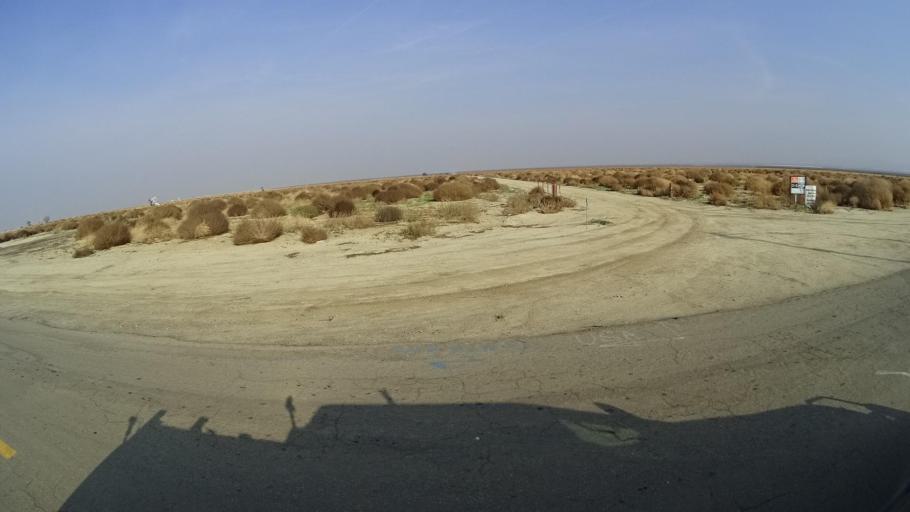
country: US
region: California
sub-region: Kern County
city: Lebec
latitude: 34.9930
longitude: -118.8823
